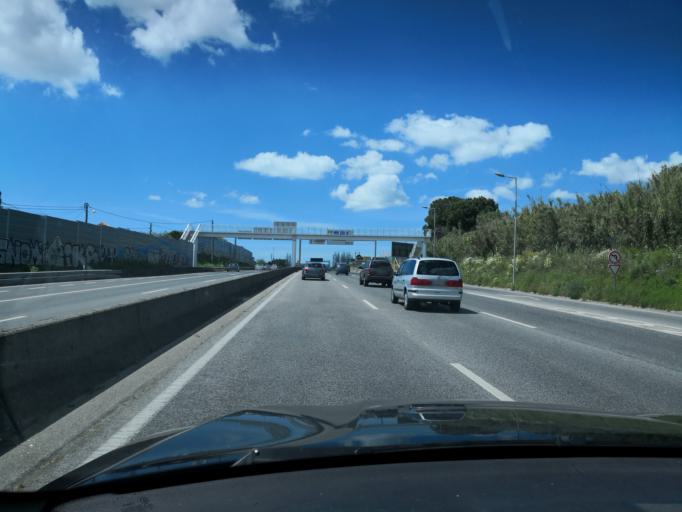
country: PT
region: Setubal
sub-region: Almada
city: Caparica
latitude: 38.6603
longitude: -9.1913
